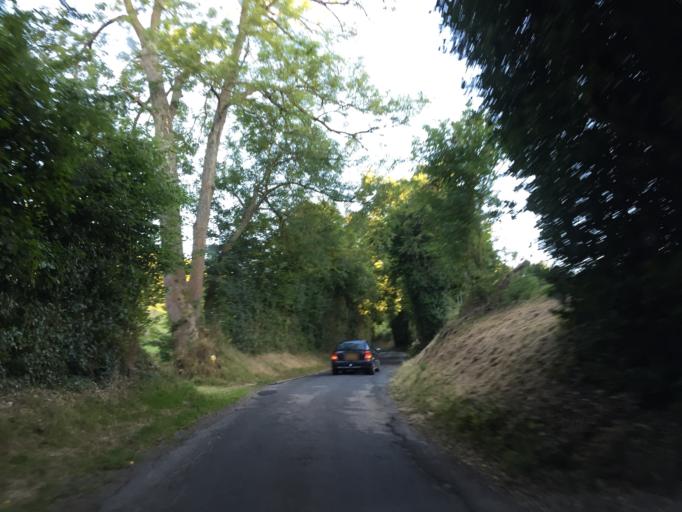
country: FR
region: Lower Normandy
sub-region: Departement du Calvados
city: Equemauville
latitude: 49.4071
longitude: 0.2053
